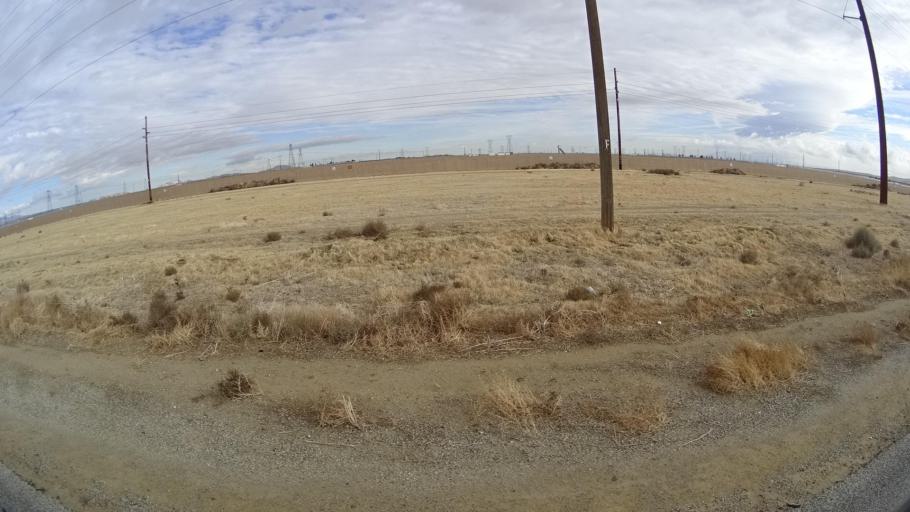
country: US
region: California
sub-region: Los Angeles County
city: Green Valley
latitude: 34.8300
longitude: -118.4314
